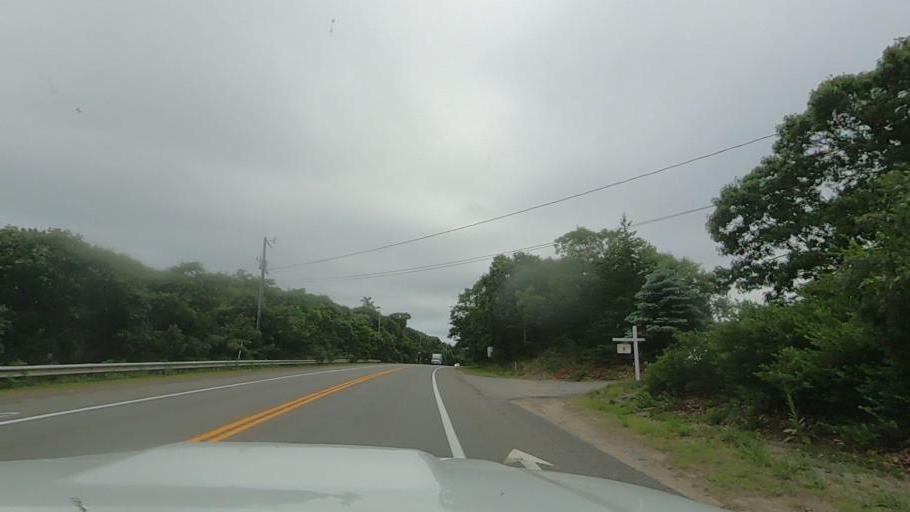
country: US
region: Massachusetts
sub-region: Barnstable County
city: Truro
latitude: 42.0012
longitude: -70.0509
